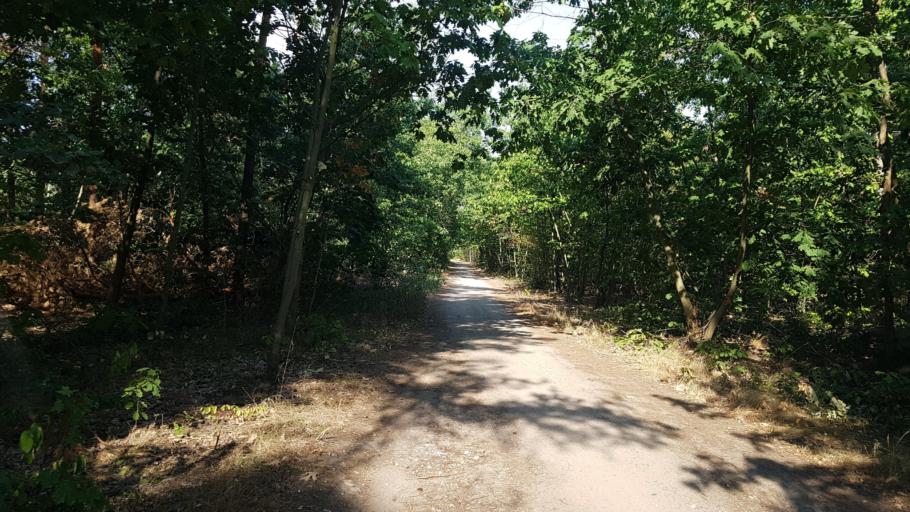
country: DE
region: Brandenburg
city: Sallgast
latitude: 51.5898
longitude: 13.8396
